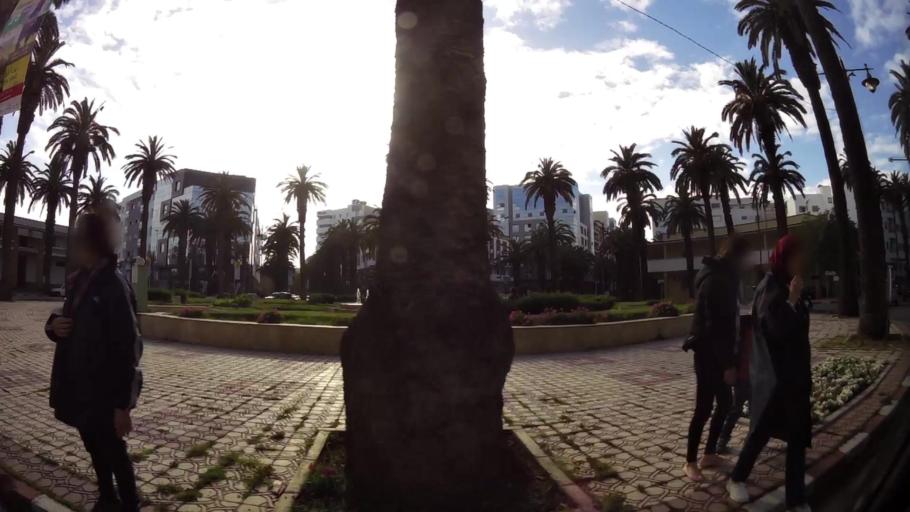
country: MA
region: Grand Casablanca
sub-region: Mohammedia
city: Mohammedia
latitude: 33.7041
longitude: -7.3946
